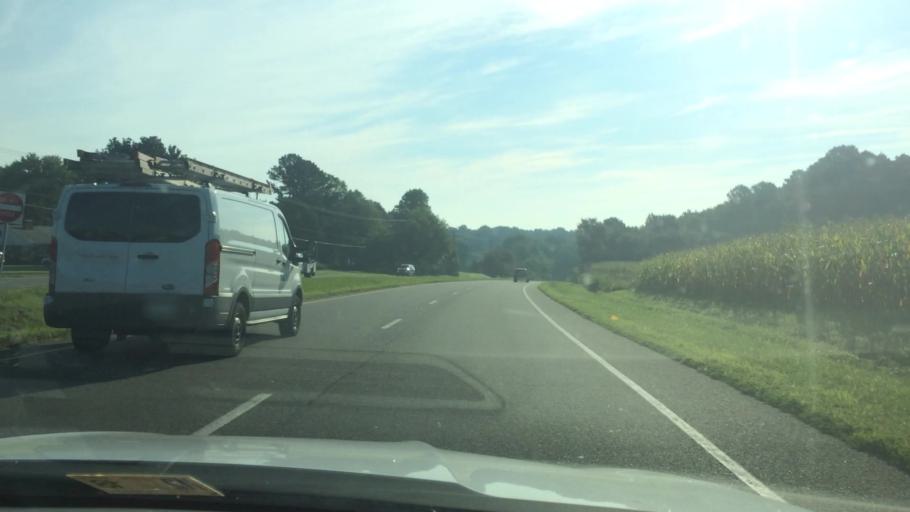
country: US
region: Virginia
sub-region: Gloucester County
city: Gloucester Courthouse
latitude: 37.4255
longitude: -76.5029
